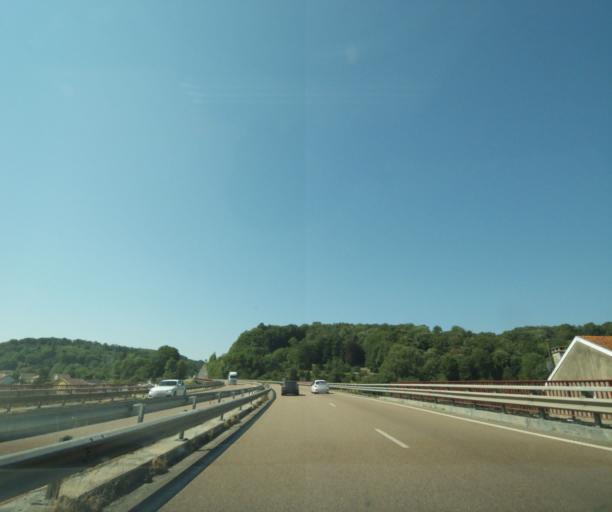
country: FR
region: Lorraine
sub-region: Departement de la Meuse
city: Ligny-en-Barrois
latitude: 48.6920
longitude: 5.3183
